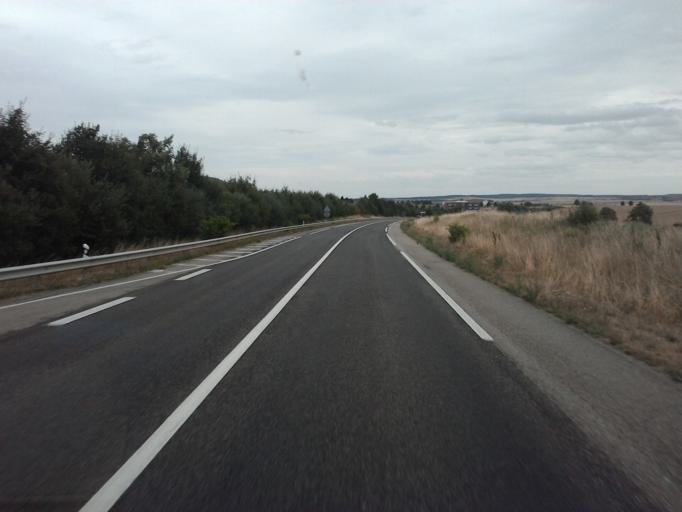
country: FR
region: Lorraine
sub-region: Departement de Meurthe-et-Moselle
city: Bainville-sur-Madon
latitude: 48.5801
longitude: 6.0429
